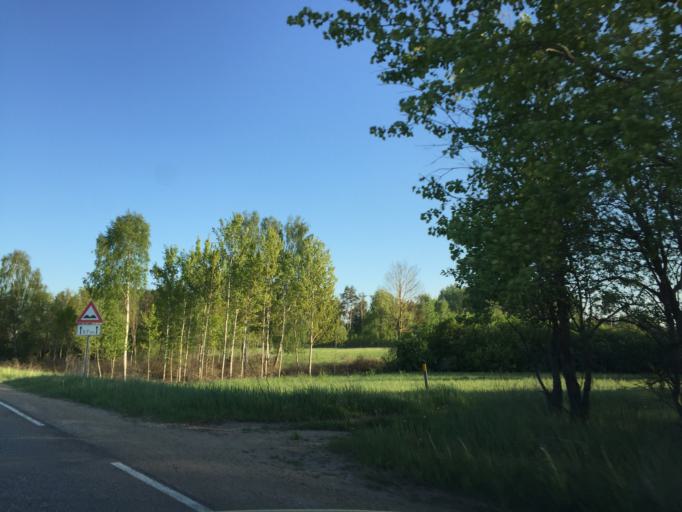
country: LV
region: Baldone
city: Baldone
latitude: 56.7674
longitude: 24.3080
